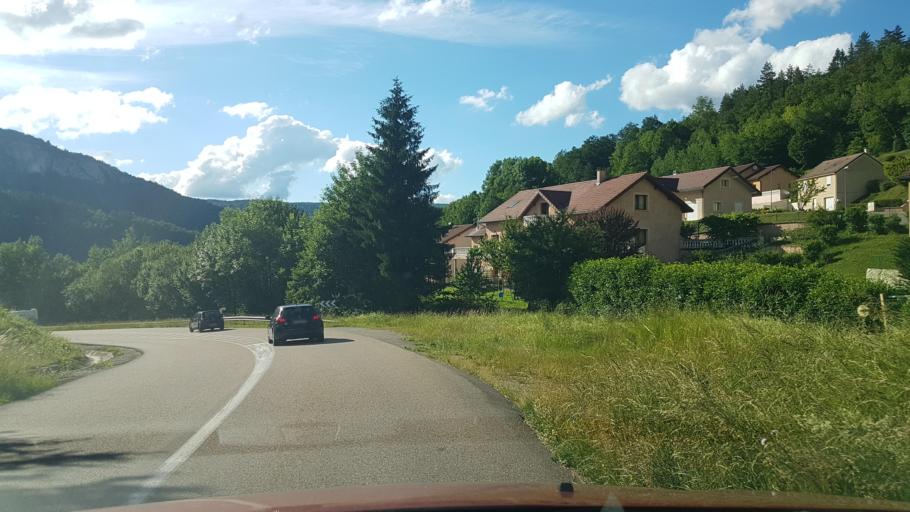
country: FR
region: Franche-Comte
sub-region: Departement du Jura
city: Saint-Claude
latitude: 46.3685
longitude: 5.8815
